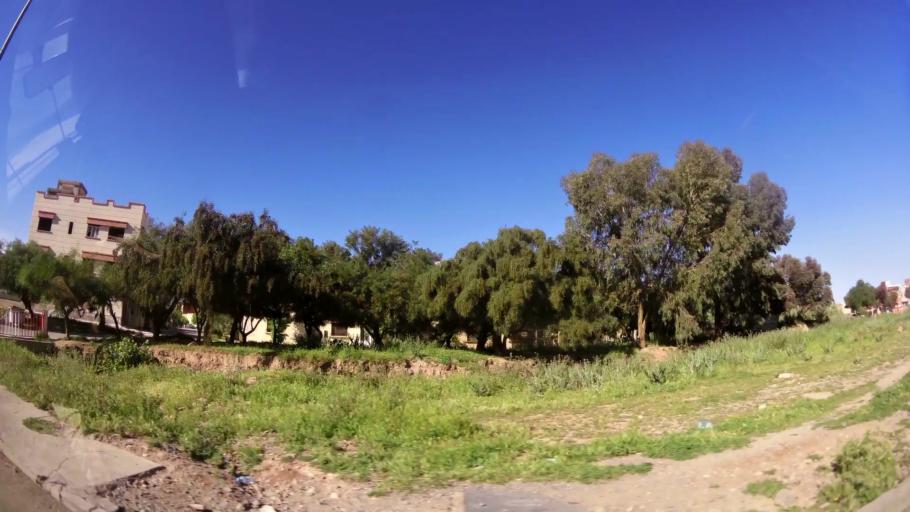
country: MA
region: Oriental
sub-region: Oujda-Angad
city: Oujda
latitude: 34.6553
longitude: -1.8903
